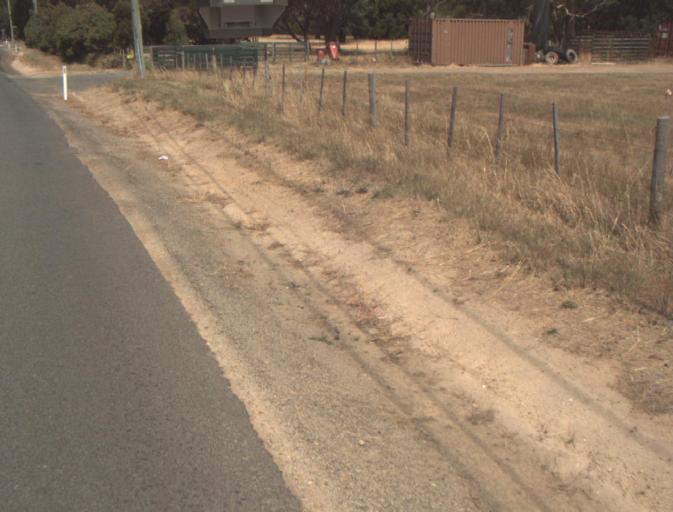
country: AU
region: Tasmania
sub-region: Launceston
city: Newstead
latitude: -41.4864
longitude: 147.1941
